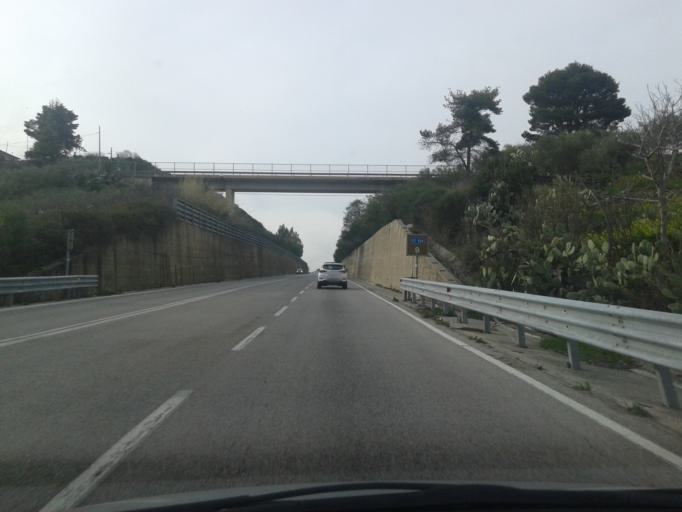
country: IT
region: Sicily
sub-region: Palermo
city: Giacalone
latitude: 38.0317
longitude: 13.2574
